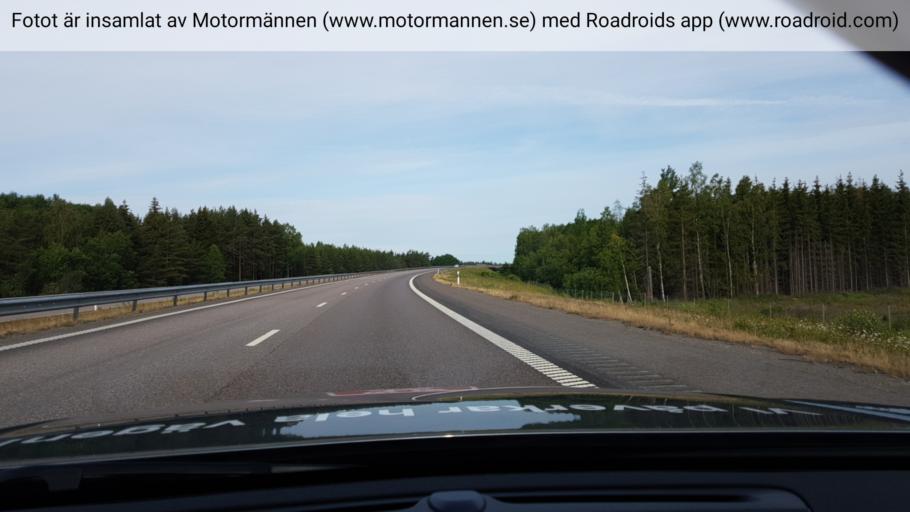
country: SE
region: Soedermanland
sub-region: Nykopings Kommun
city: Svalsta
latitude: 58.7500
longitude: 16.8844
